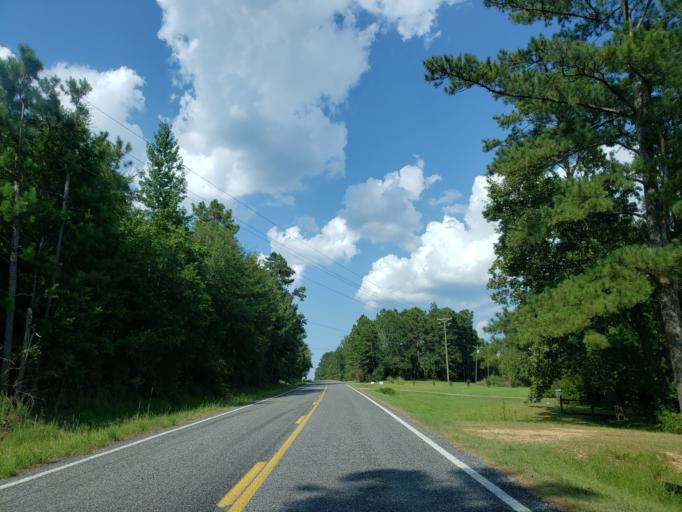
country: US
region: Mississippi
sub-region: Covington County
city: Collins
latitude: 31.6056
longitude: -89.4381
